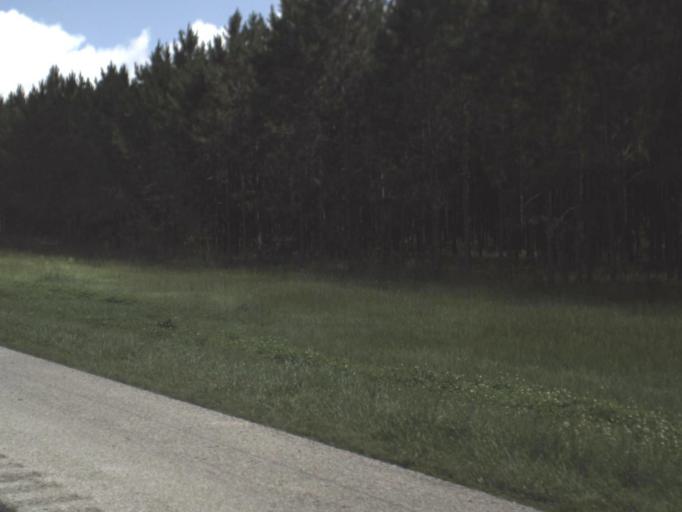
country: US
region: Florida
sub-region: Alachua County
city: High Springs
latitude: 29.8560
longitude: -82.5376
